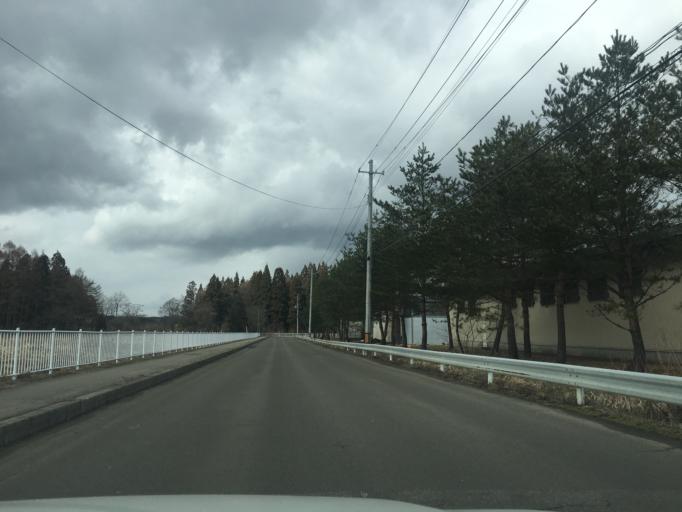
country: JP
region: Akita
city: Takanosu
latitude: 40.1847
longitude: 140.3406
